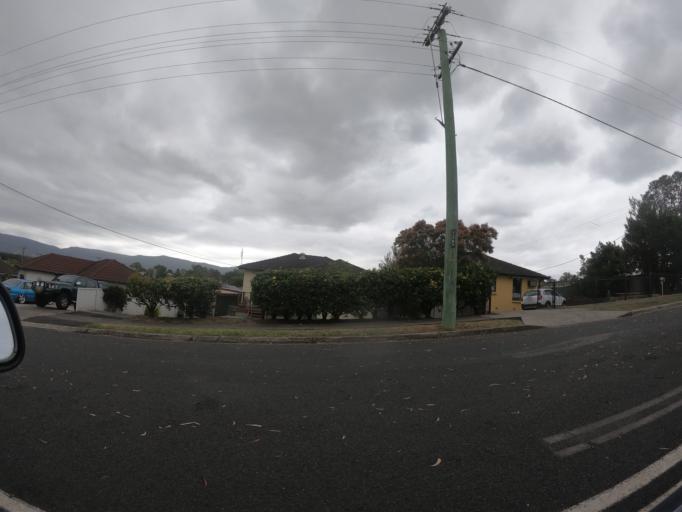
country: AU
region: New South Wales
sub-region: Wollongong
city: Berkeley
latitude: -34.4817
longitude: 150.8428
